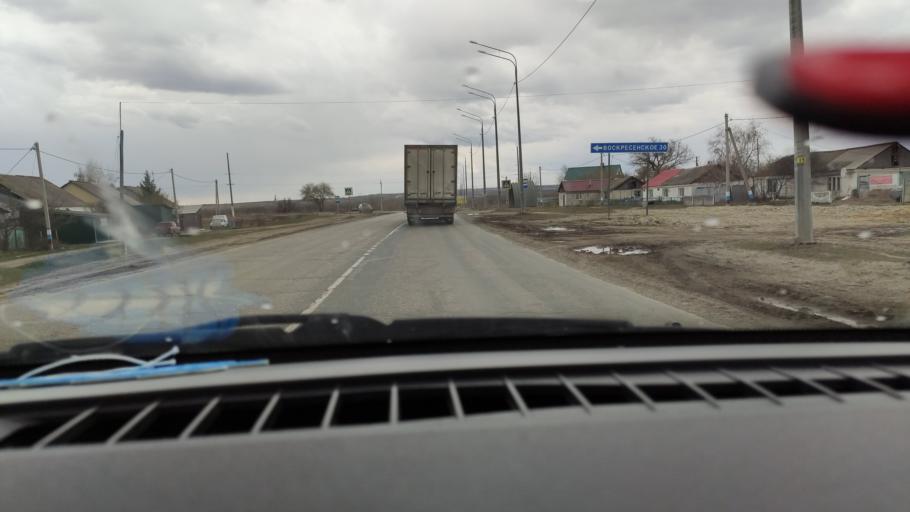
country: RU
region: Saratov
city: Sinodskoye
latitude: 51.9806
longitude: 46.6560
